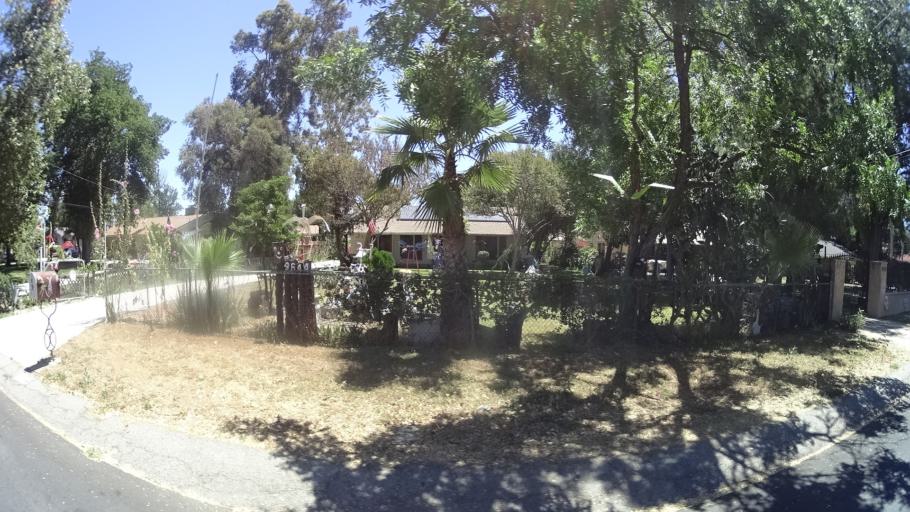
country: US
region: California
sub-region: Los Angeles County
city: San Fernando
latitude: 34.2460
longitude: -118.4719
